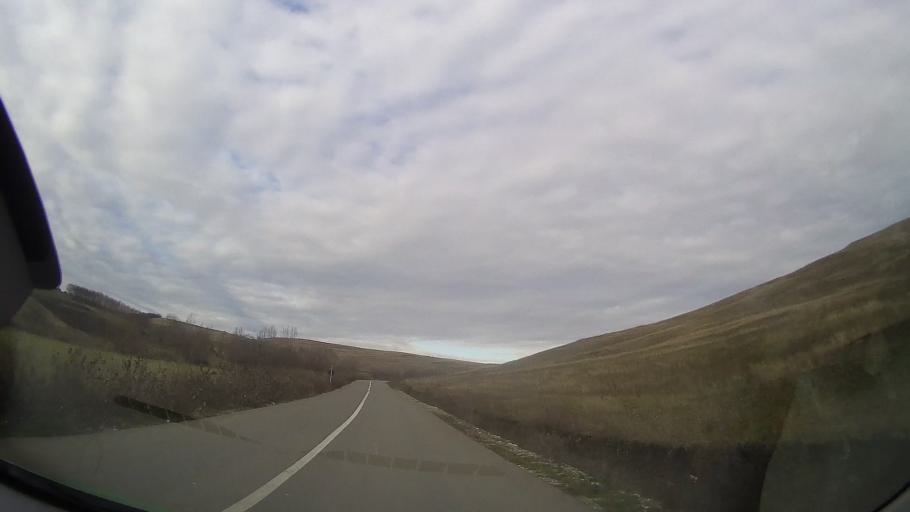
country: RO
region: Bistrita-Nasaud
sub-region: Comuna Silvasu de Campie
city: Silvasu de Campie
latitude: 46.8067
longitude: 24.2965
